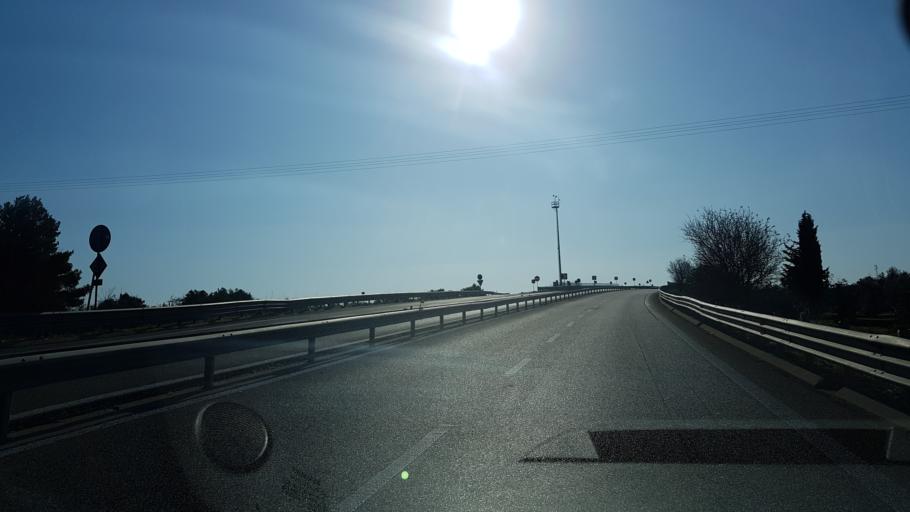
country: IT
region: Apulia
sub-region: Provincia di Lecce
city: Galatone
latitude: 40.1313
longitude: 18.0530
